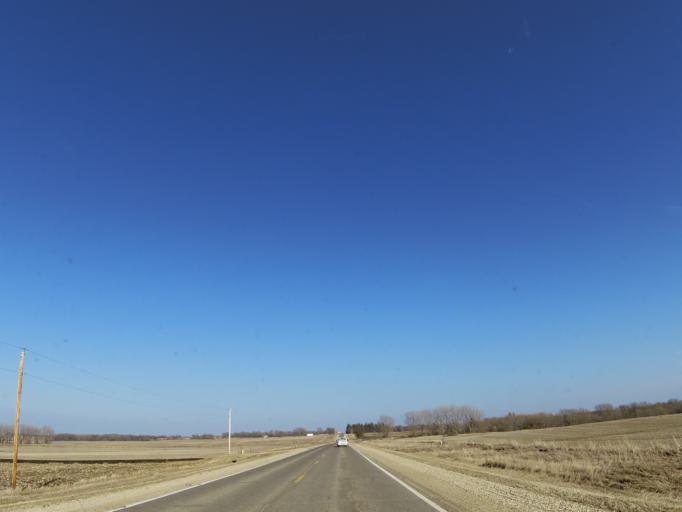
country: US
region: Iowa
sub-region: Worth County
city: Northwood
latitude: 43.4442
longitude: -93.2871
